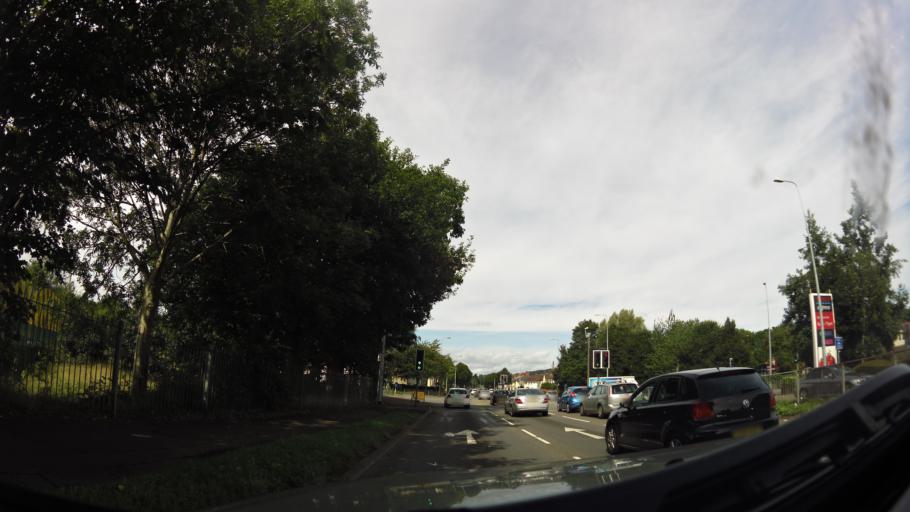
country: GB
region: Wales
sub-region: Cardiff
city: Radyr
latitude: 51.5166
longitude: -3.2162
